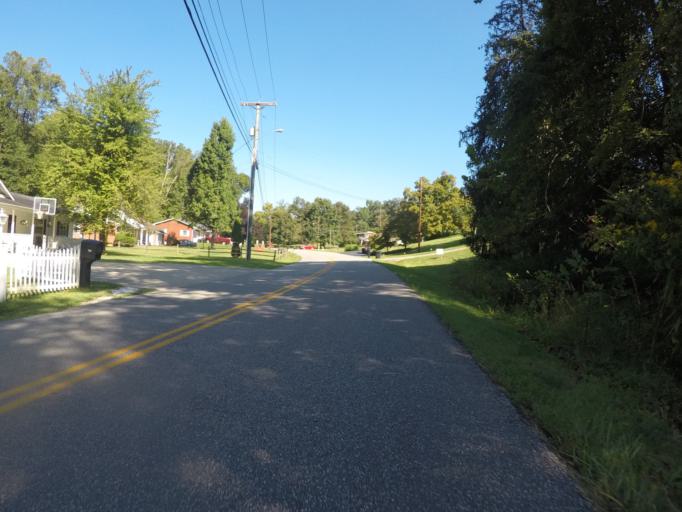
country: US
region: Kentucky
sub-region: Greenup County
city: Russell
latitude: 38.5128
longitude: -82.6934
